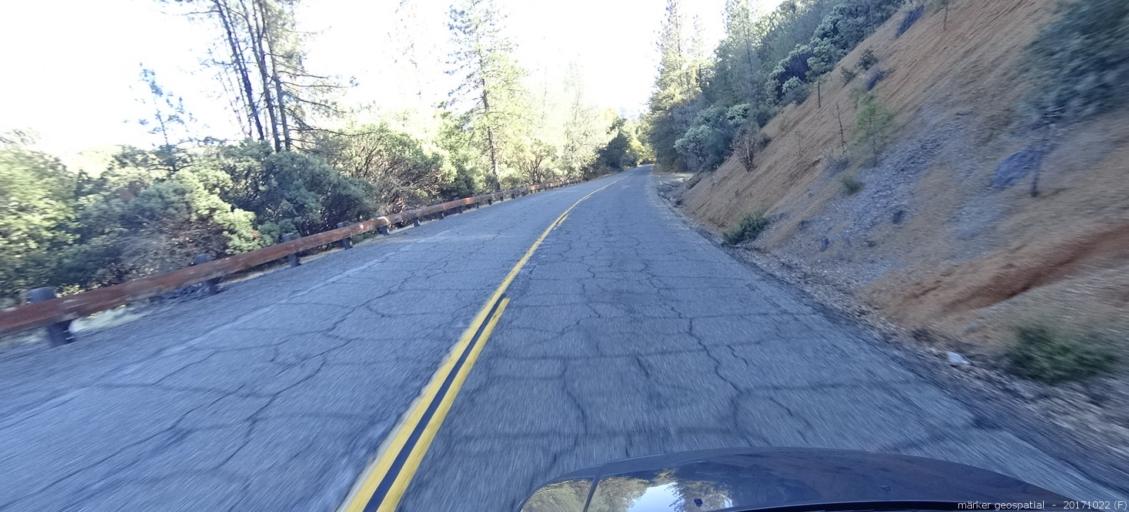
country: US
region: California
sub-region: Shasta County
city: Shasta Lake
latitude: 40.8623
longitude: -122.3585
